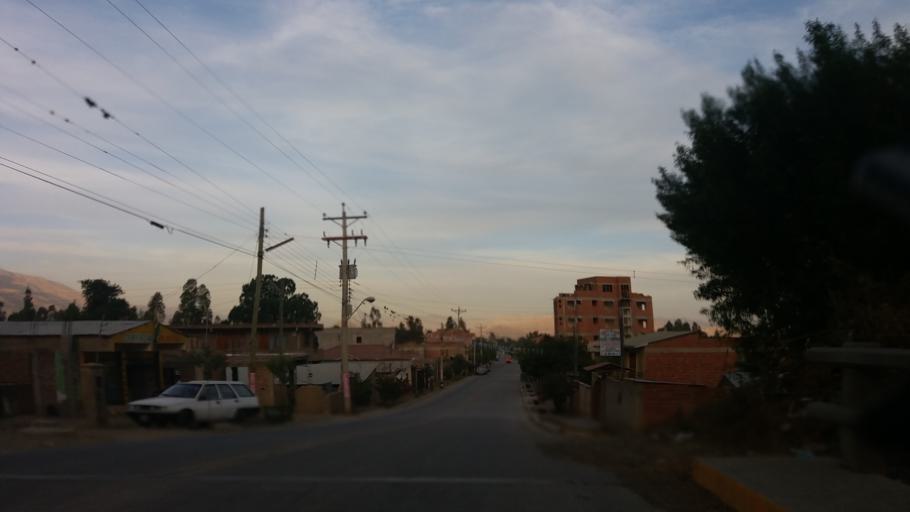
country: BO
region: Cochabamba
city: Cochabamba
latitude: -17.3646
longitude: -66.2196
